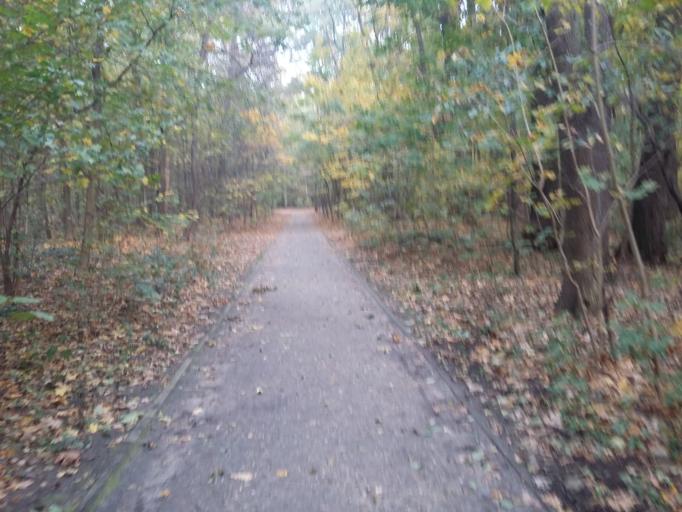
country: PL
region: Lodz Voivodeship
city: Lodz
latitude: 51.7604
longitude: 19.4203
